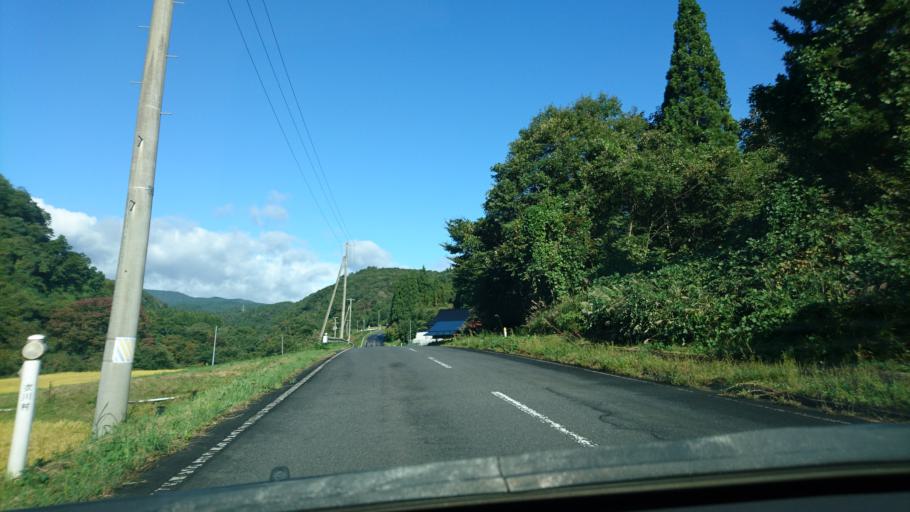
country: JP
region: Iwate
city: Ichinoseki
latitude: 39.0213
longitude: 141.0215
